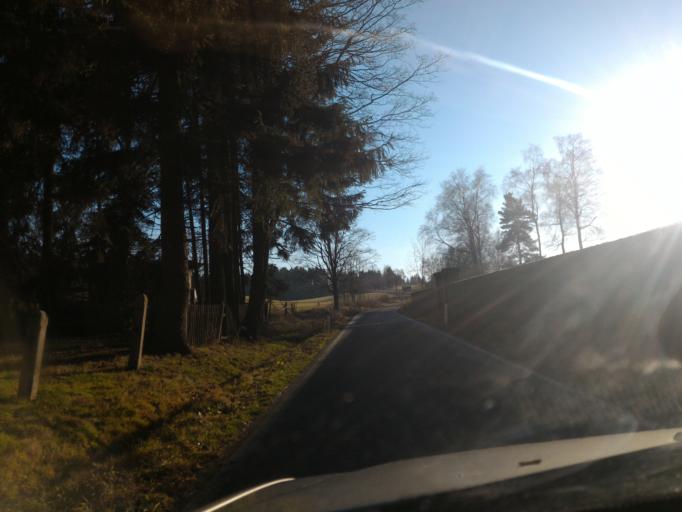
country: DE
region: Saxony
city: Kurort Jonsdorf
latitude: 50.8266
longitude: 14.7007
